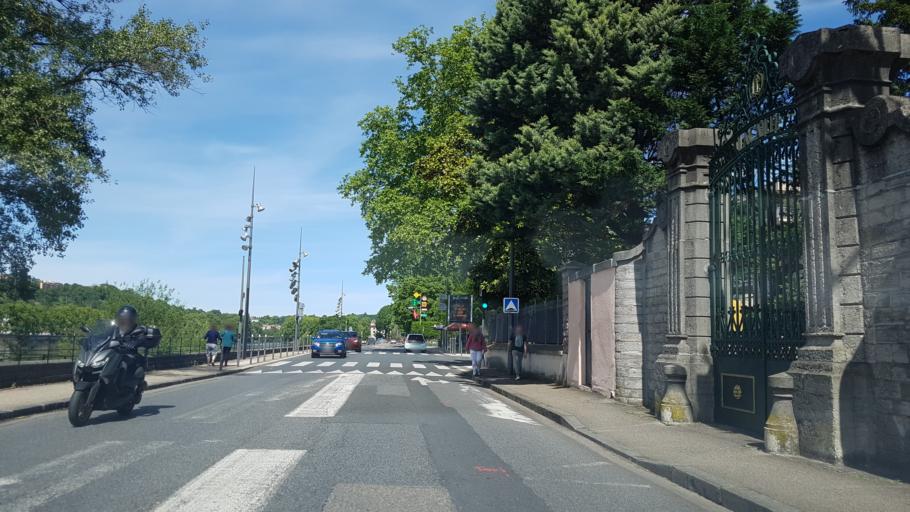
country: FR
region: Rhone-Alpes
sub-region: Departement du Rhone
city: Caluire-et-Cuire
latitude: 45.7913
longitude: 4.8226
